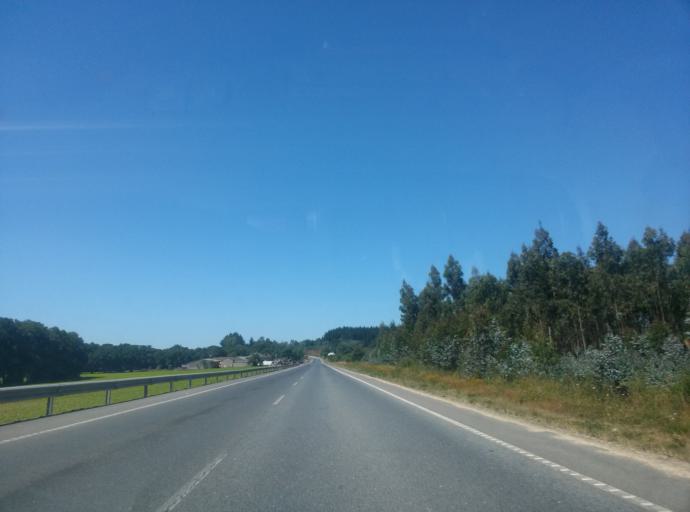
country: ES
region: Galicia
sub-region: Provincia de Lugo
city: Mos
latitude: 43.1192
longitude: -7.4855
